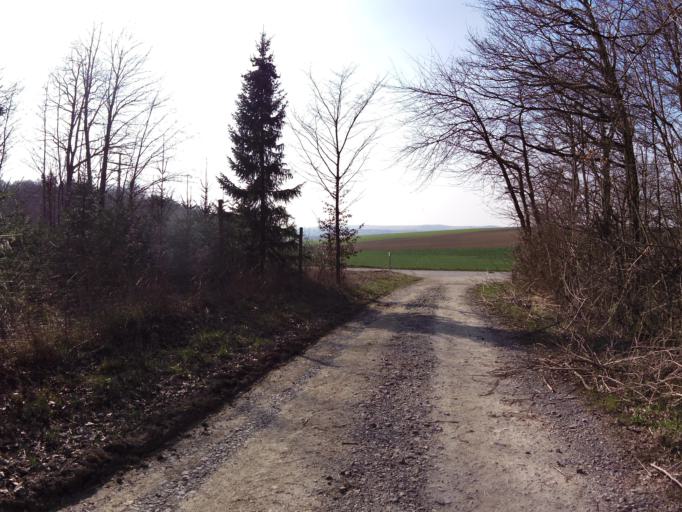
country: DE
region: Bavaria
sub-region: Regierungsbezirk Unterfranken
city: Rottendorf
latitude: 49.8134
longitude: 10.0297
